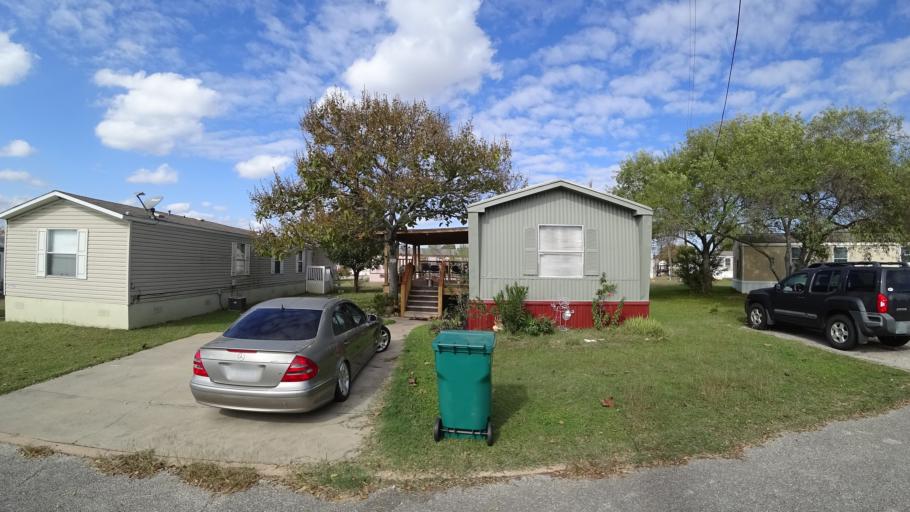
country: US
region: Texas
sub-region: Travis County
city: Pflugerville
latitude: 30.4332
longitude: -97.6423
